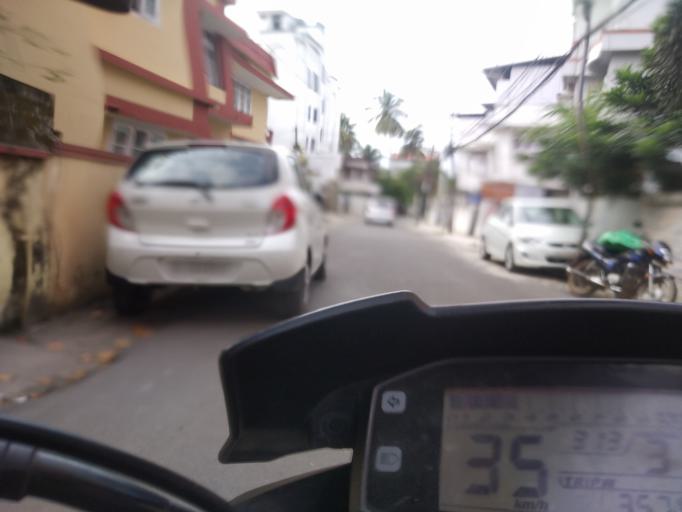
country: IN
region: Kerala
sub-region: Ernakulam
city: Cochin
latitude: 9.9718
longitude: 76.2881
